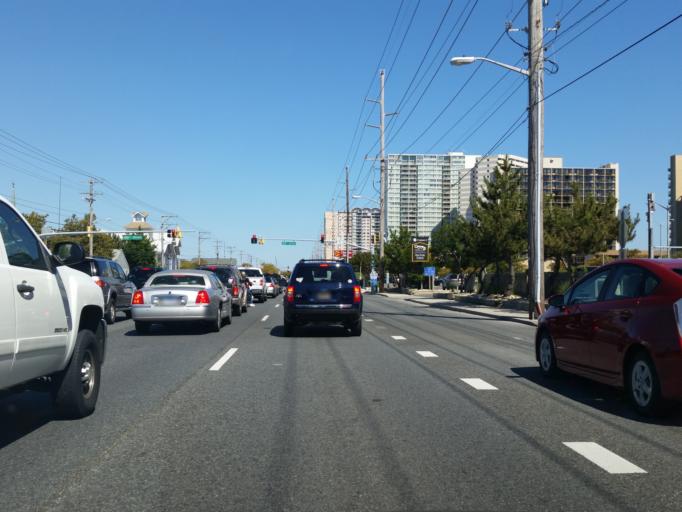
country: US
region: Maryland
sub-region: Worcester County
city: Ocean City
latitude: 38.4119
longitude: -75.0581
